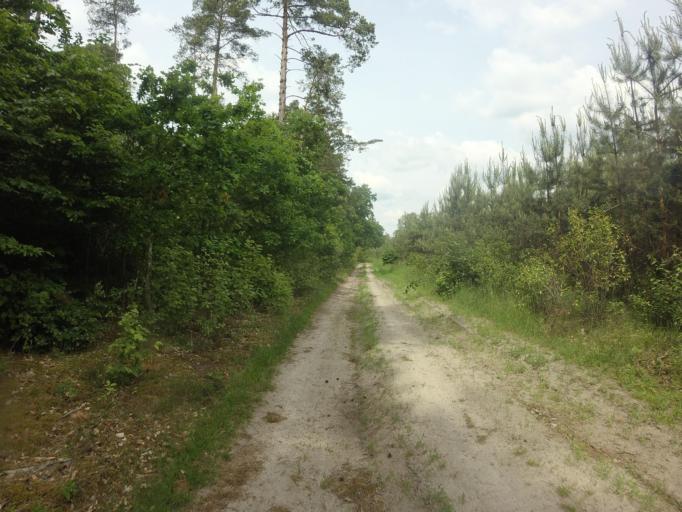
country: PL
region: West Pomeranian Voivodeship
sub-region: Powiat stargardzki
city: Dobrzany
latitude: 53.3054
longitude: 15.4647
